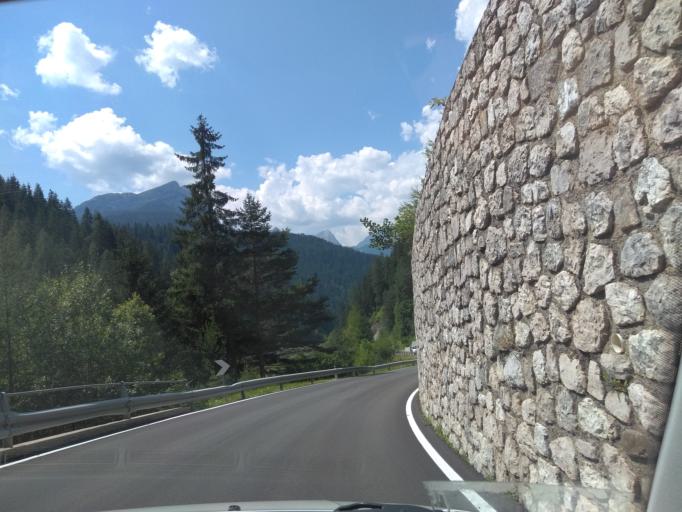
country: IT
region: Veneto
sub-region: Provincia di Belluno
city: Colle Santa Lucia
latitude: 46.4405
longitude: 12.0123
